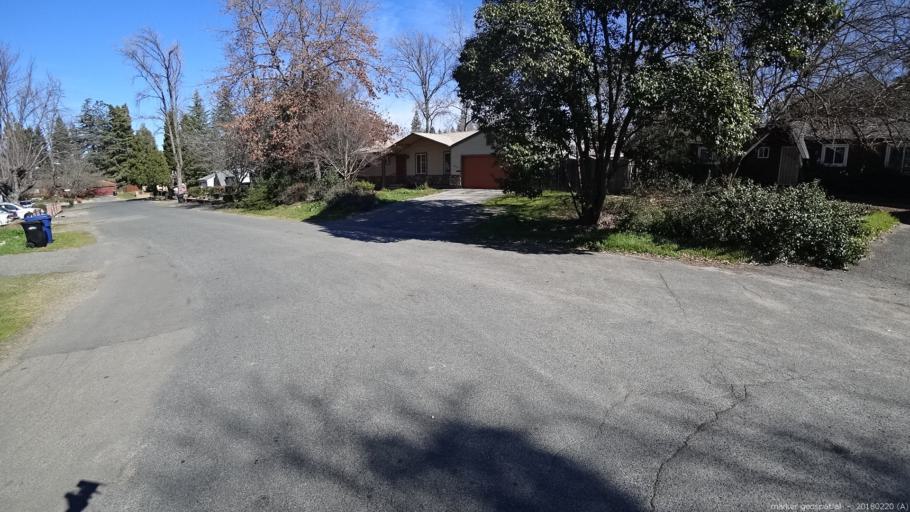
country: US
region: California
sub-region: Sacramento County
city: Orangevale
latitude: 38.6807
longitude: -121.2221
